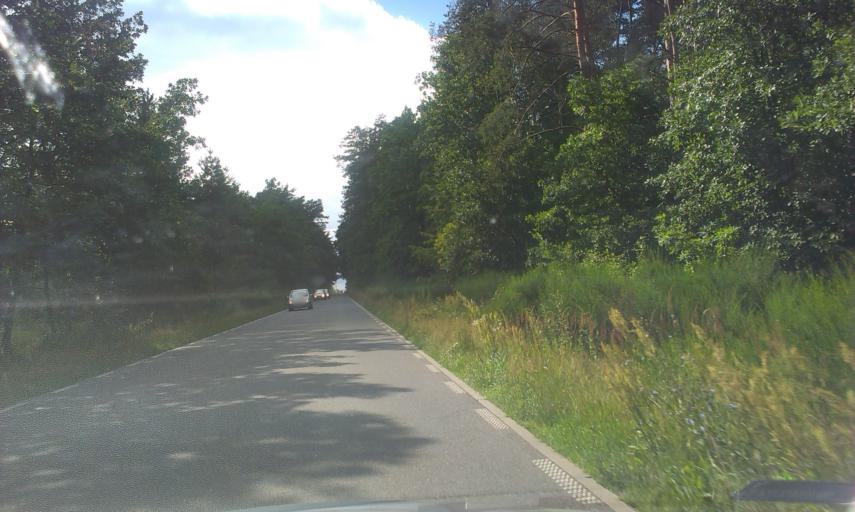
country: PL
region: Masovian Voivodeship
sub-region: Powiat zyrardowski
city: Radziejowice
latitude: 51.9683
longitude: 20.5875
